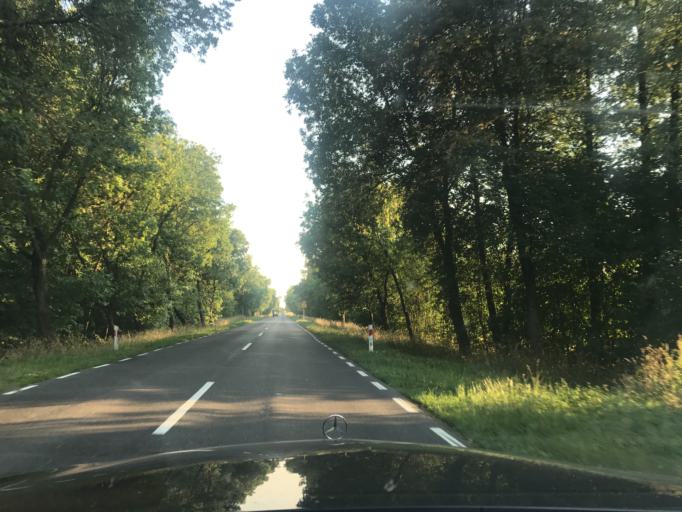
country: PL
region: Lublin Voivodeship
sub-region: Powiat parczewski
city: Debowa Kloda
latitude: 51.6625
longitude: 23.0072
